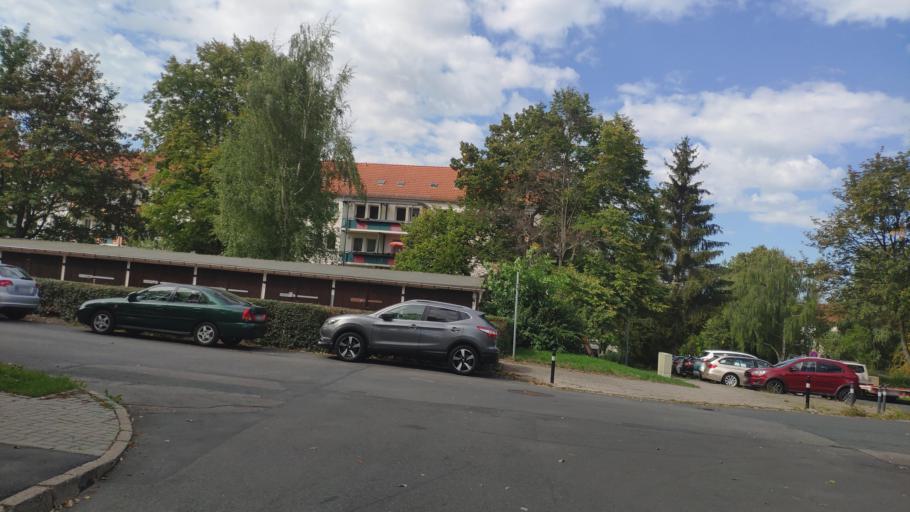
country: DE
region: Saxony
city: Chemnitz
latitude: 50.8199
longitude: 12.9025
